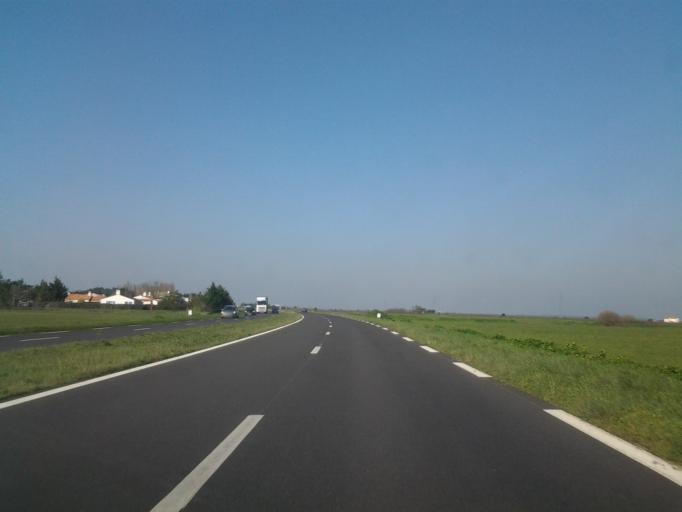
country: FR
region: Pays de la Loire
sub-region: Departement de la Vendee
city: Barbatre
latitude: 46.9527
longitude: -2.1793
